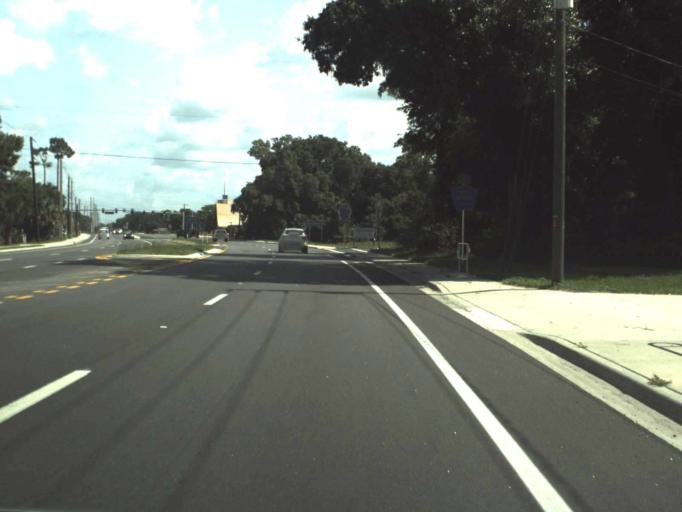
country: US
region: Florida
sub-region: Seminole County
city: Midway
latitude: 28.8475
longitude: -81.1621
